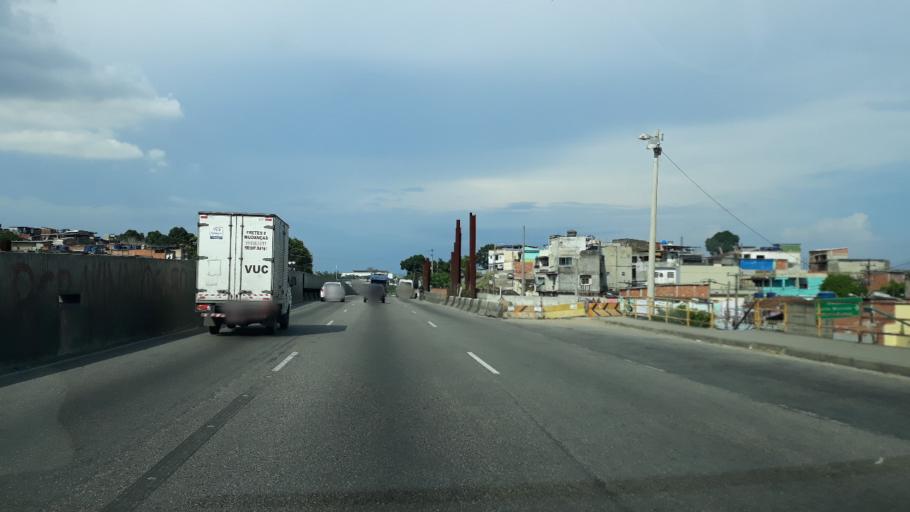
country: BR
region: Rio de Janeiro
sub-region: Sao Joao De Meriti
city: Sao Joao de Meriti
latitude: -22.8369
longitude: -43.3639
